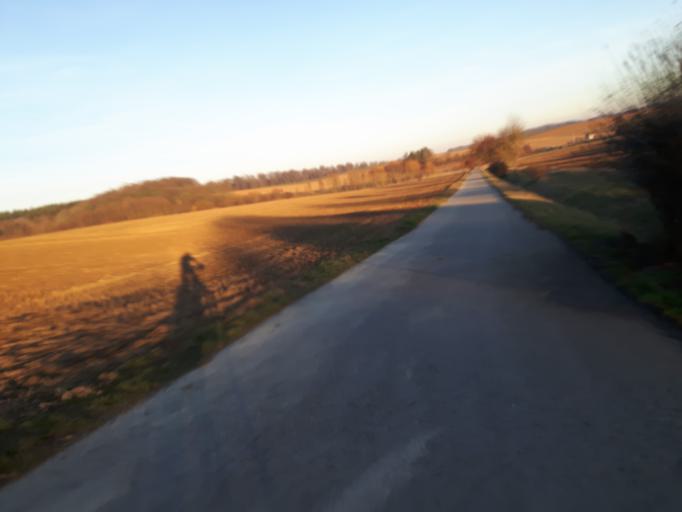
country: DE
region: Baden-Wuerttemberg
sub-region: Regierungsbezirk Stuttgart
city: Massenbachhausen
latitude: 49.1816
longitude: 9.0501
